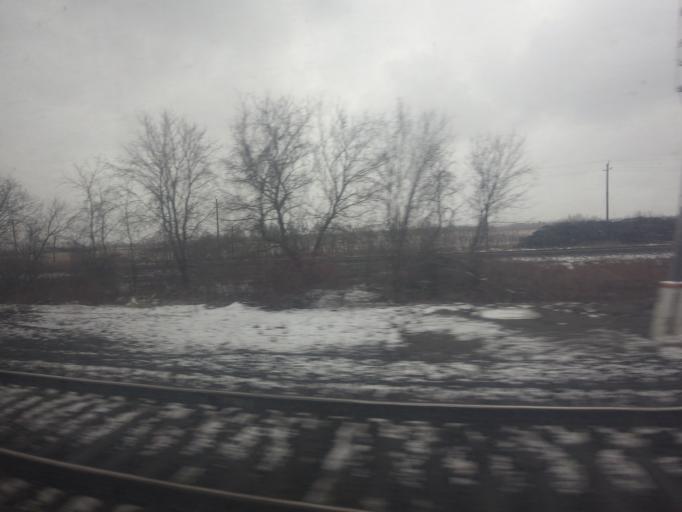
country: CA
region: Ontario
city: Quinte West
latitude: 44.0427
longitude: -77.7183
